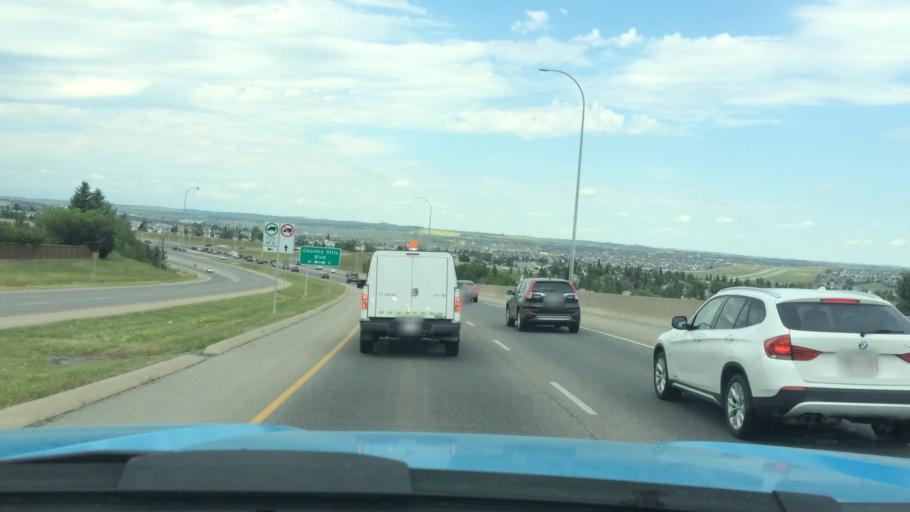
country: CA
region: Alberta
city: Calgary
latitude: 51.1384
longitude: -114.1210
